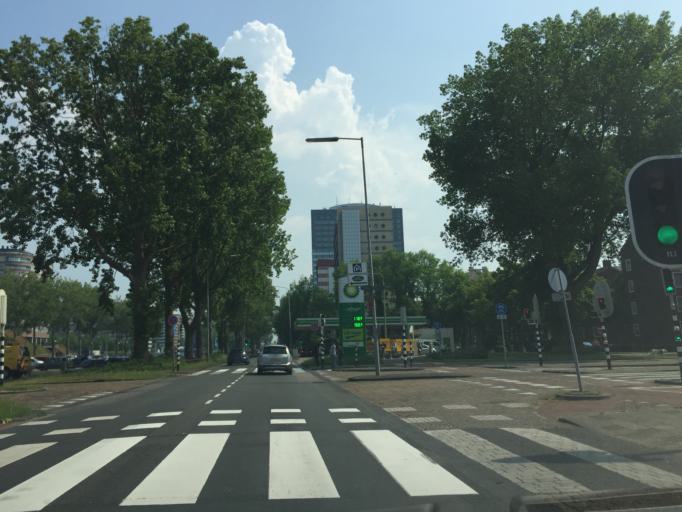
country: NL
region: South Holland
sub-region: Gemeente Rijswijk
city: Rijswijk
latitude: 52.0371
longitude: 4.3122
